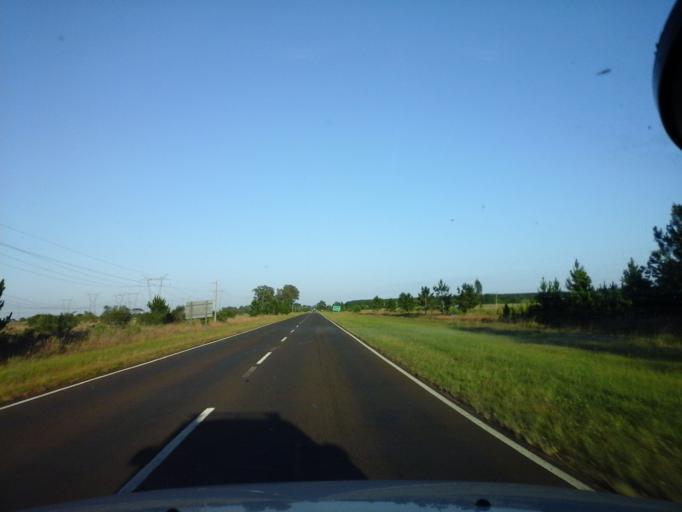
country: AR
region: Corrientes
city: Ituzaingo
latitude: -27.5728
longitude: -56.5193
